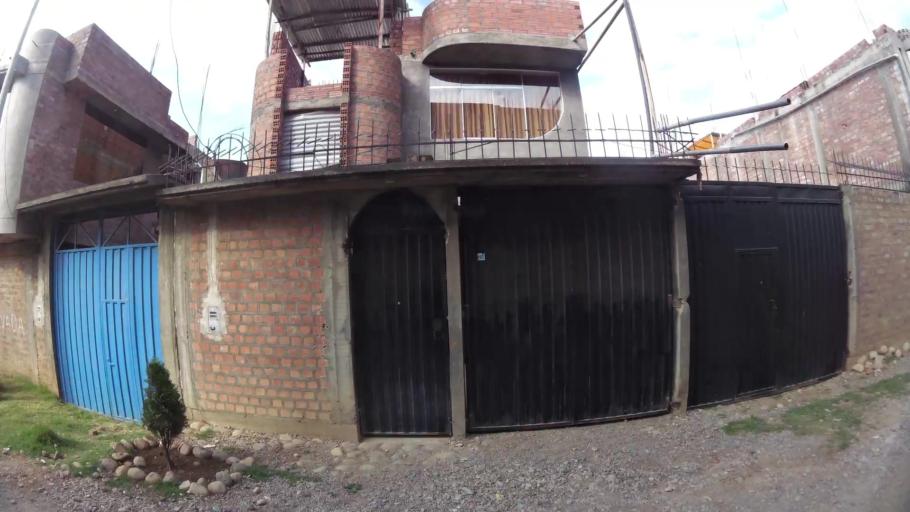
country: PE
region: Junin
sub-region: Provincia de Huancayo
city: Huancayo
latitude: -12.0523
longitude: -75.1962
